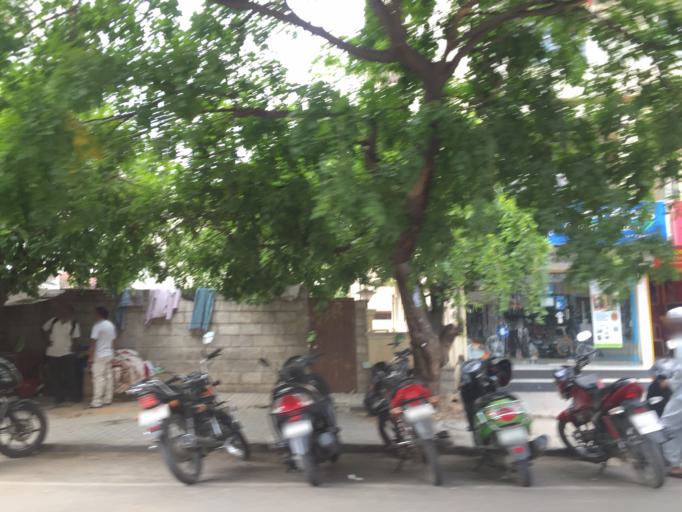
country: IN
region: Karnataka
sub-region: Bangalore Urban
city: Bangalore
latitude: 13.0213
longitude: 77.6418
